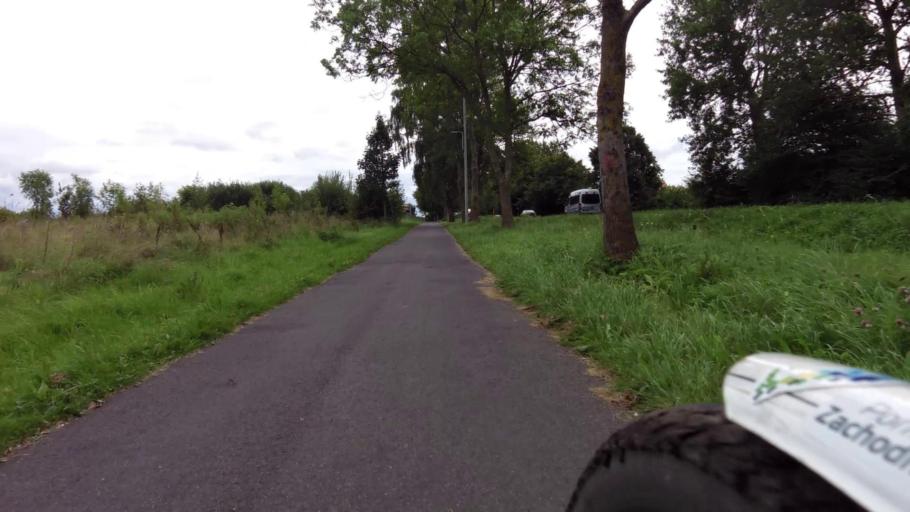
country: PL
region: West Pomeranian Voivodeship
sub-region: Powiat koszalinski
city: Mielno
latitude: 54.2474
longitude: 16.0629
